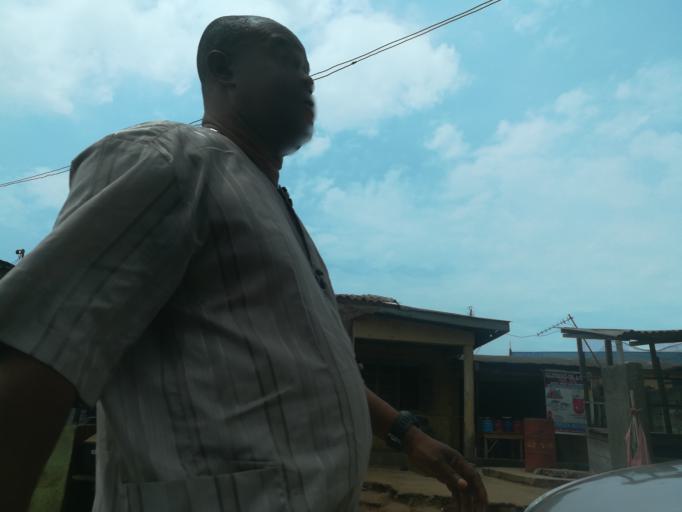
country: NG
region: Lagos
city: Ikorodu
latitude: 6.6121
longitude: 3.5124
